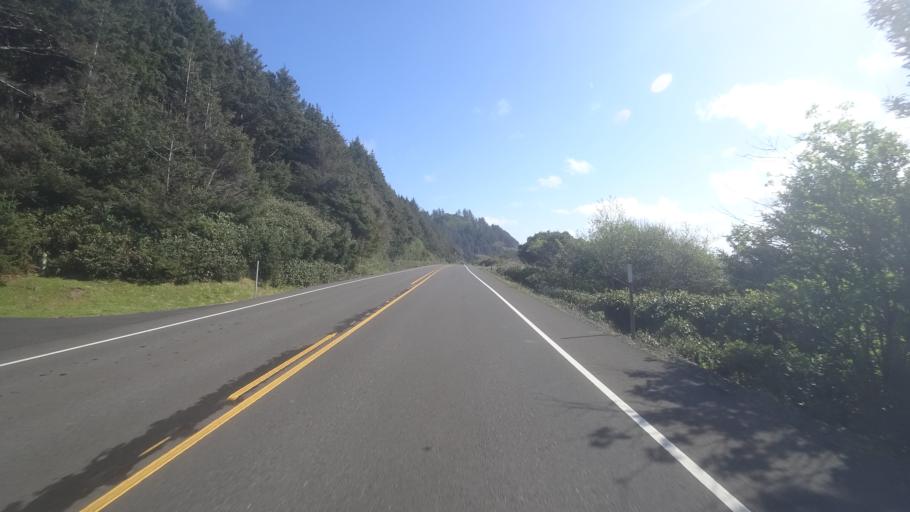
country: US
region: Oregon
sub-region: Lincoln County
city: Waldport
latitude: 44.2132
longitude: -124.1133
